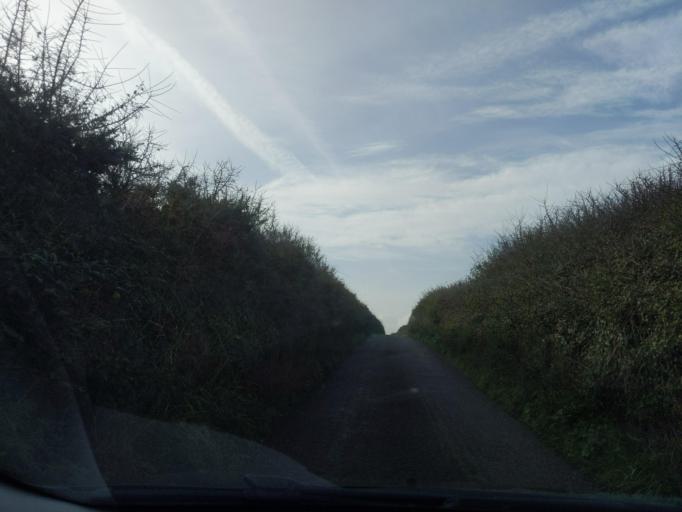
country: GB
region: England
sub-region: Cornwall
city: Pillaton
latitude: 50.3642
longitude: -4.3243
